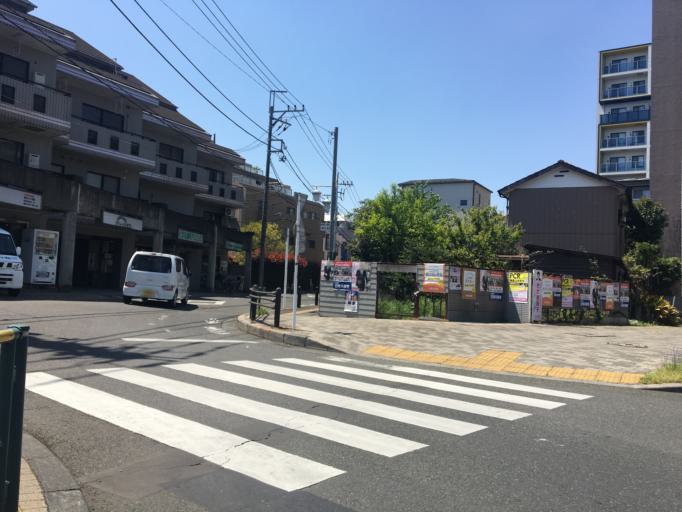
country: JP
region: Tokyo
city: Tanashicho
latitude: 35.7246
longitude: 139.5138
